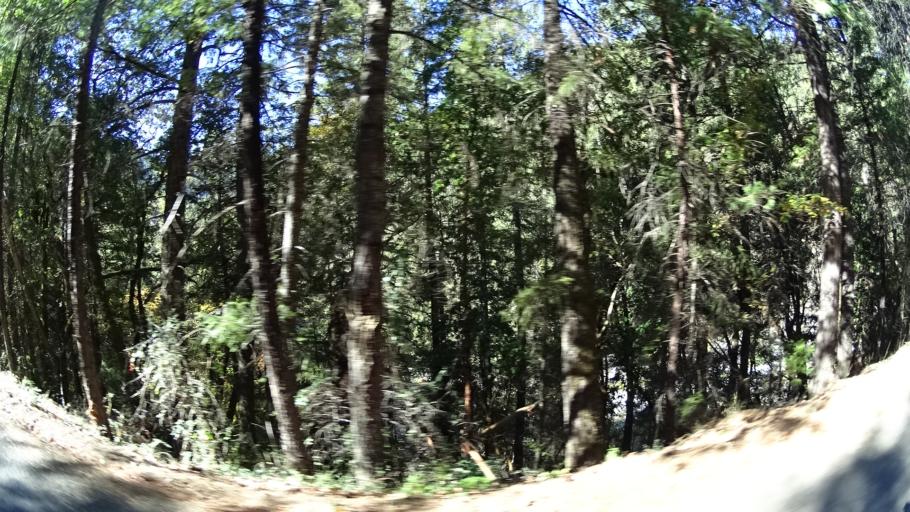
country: US
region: California
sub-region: Humboldt County
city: Willow Creek
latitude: 41.1593
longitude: -123.2070
